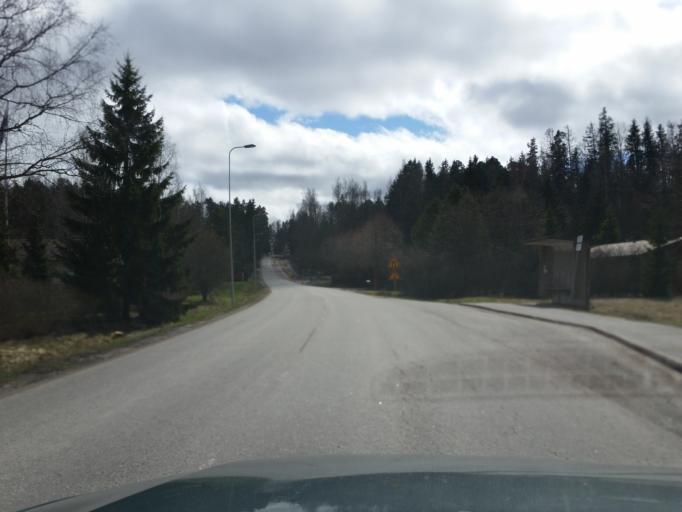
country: FI
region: Uusimaa
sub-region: Helsinki
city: Vihti
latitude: 60.4106
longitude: 24.3301
